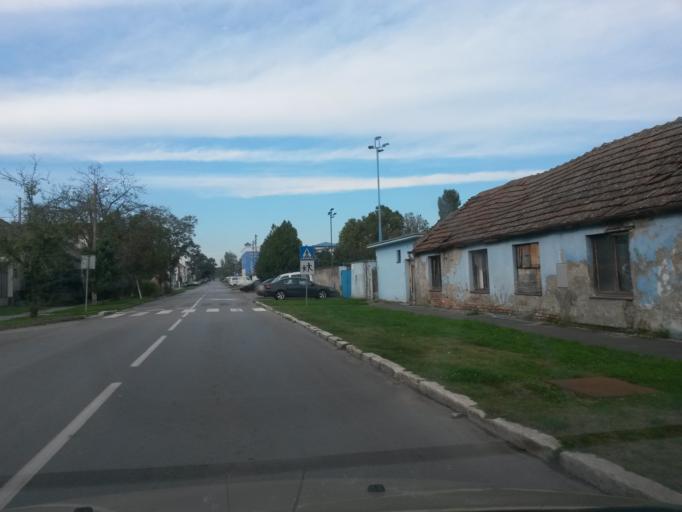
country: HR
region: Osjecko-Baranjska
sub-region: Grad Osijek
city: Osijek
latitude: 45.5552
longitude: 18.7319
